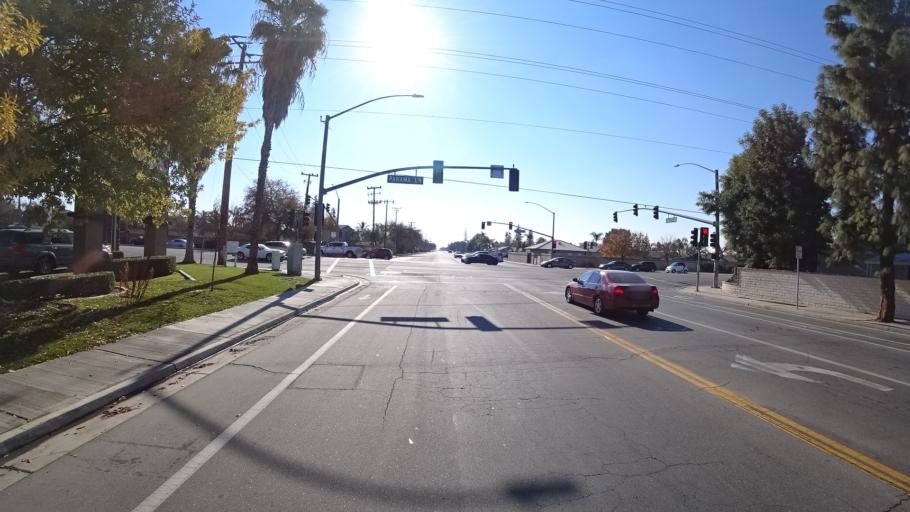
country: US
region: California
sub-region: Kern County
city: Greenfield
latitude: 35.2963
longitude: -119.0478
